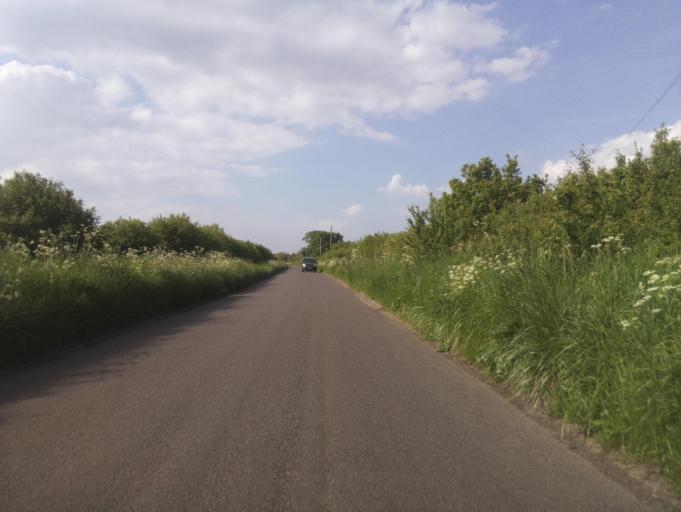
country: GB
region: England
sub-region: Wiltshire
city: Bremhill
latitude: 51.5007
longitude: -2.0735
